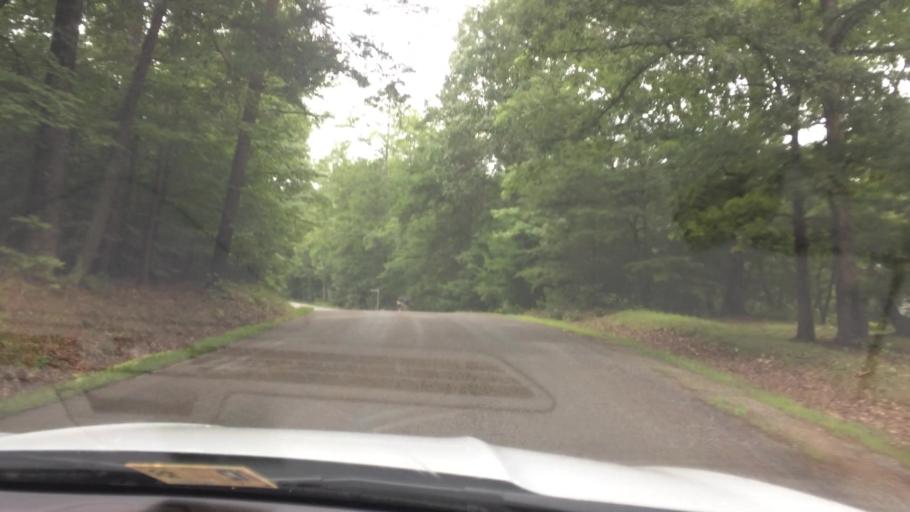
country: US
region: Virginia
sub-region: Charles City County
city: Charles City
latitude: 37.4100
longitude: -77.0498
